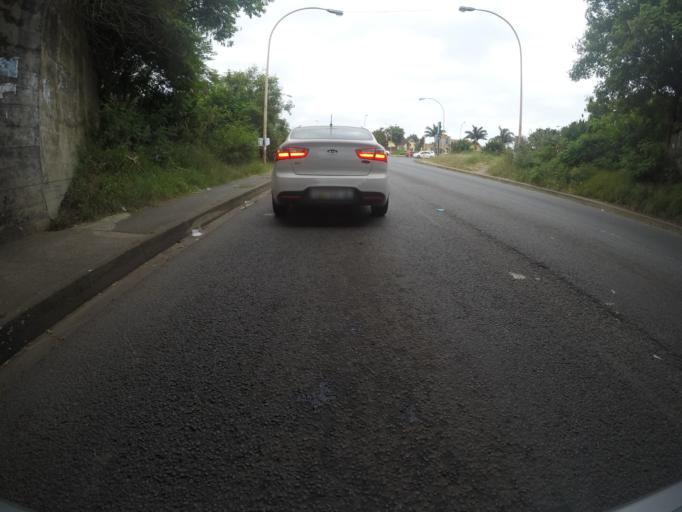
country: ZA
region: Eastern Cape
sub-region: Buffalo City Metropolitan Municipality
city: East London
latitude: -32.9840
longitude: 27.8969
